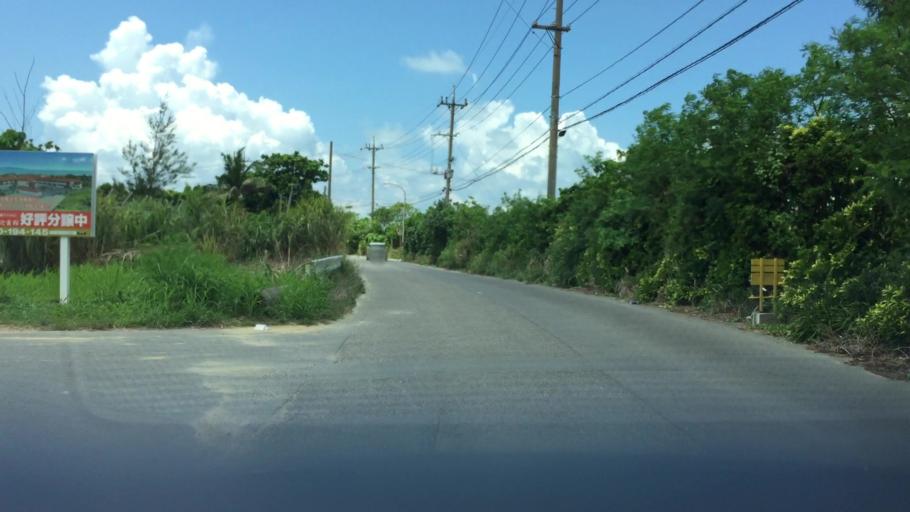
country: JP
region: Okinawa
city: Ishigaki
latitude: 24.3667
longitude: 124.1131
